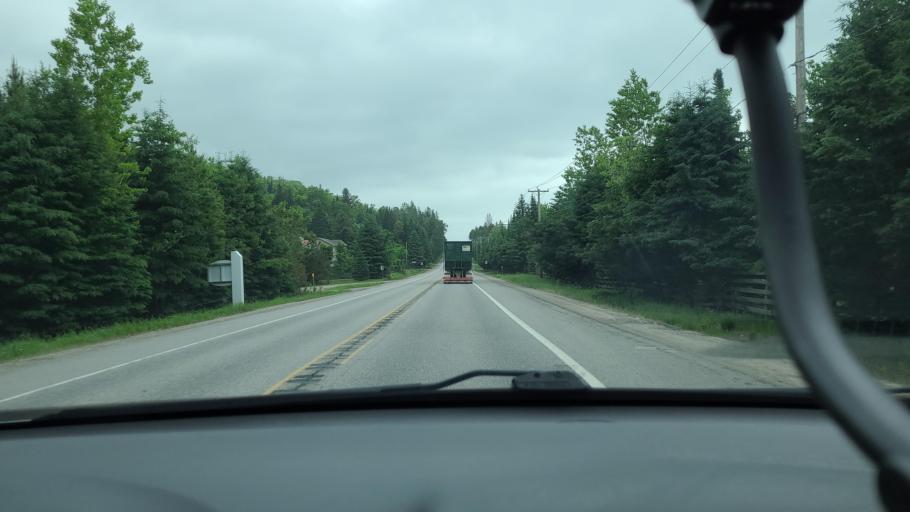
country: CA
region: Quebec
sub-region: Laurentides
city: Labelle
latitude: 46.3130
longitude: -74.7899
